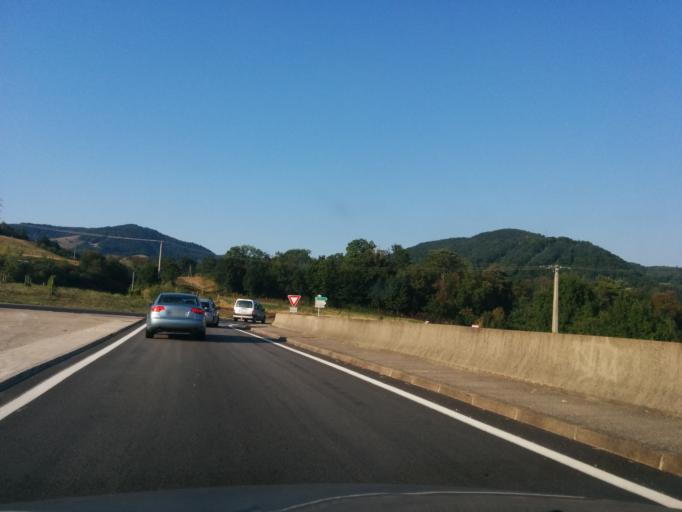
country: FR
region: Rhone-Alpes
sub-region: Departement de l'Isere
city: Voiron
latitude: 45.3786
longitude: 5.5718
